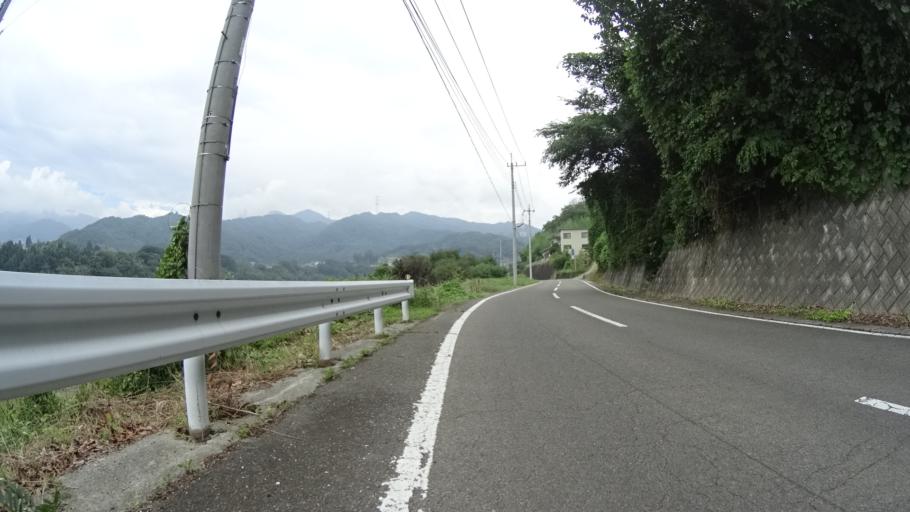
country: JP
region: Yamanashi
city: Enzan
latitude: 35.7465
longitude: 138.7228
